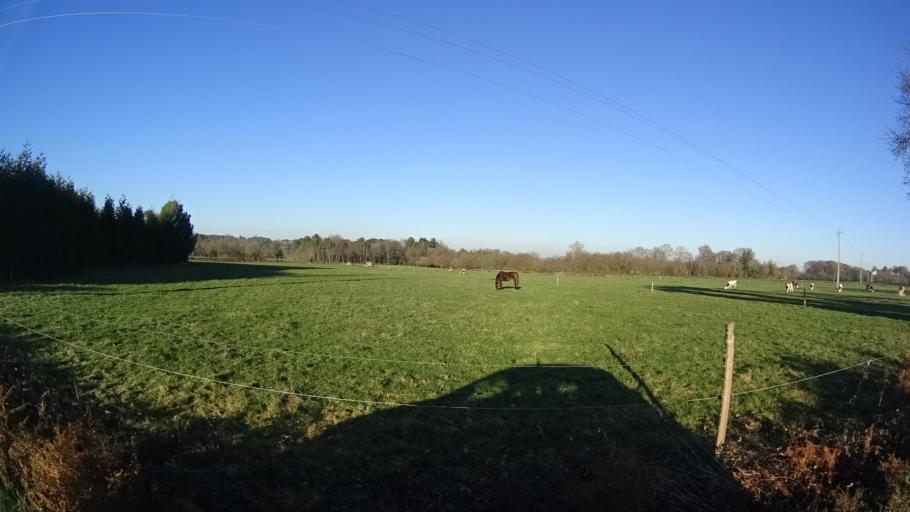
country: FR
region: Brittany
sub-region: Departement du Morbihan
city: Allaire
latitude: 47.6677
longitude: -2.1671
